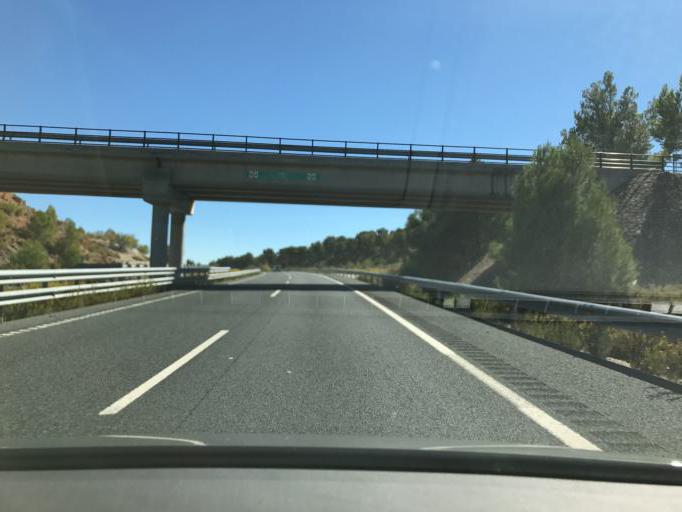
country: ES
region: Andalusia
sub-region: Provincia de Granada
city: Diezma
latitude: 37.3085
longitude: -3.3726
